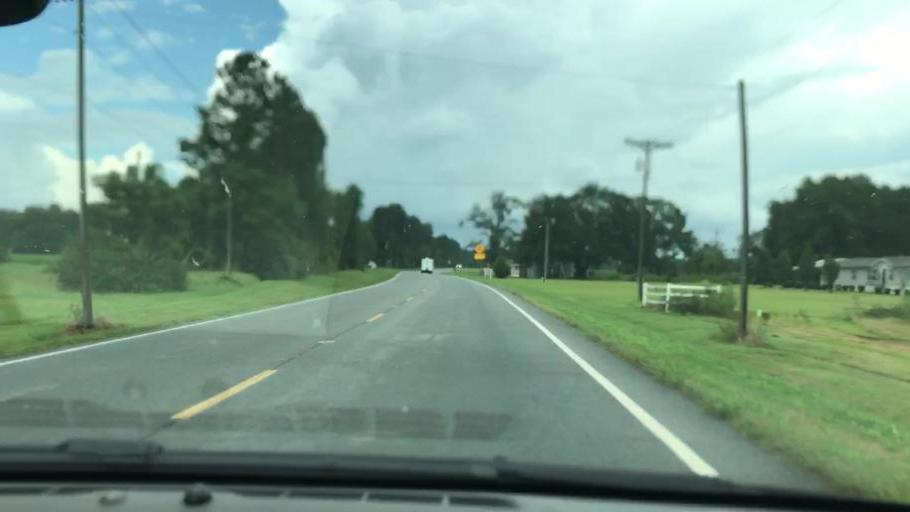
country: US
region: Georgia
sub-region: Early County
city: Blakely
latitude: 31.3800
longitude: -84.9576
